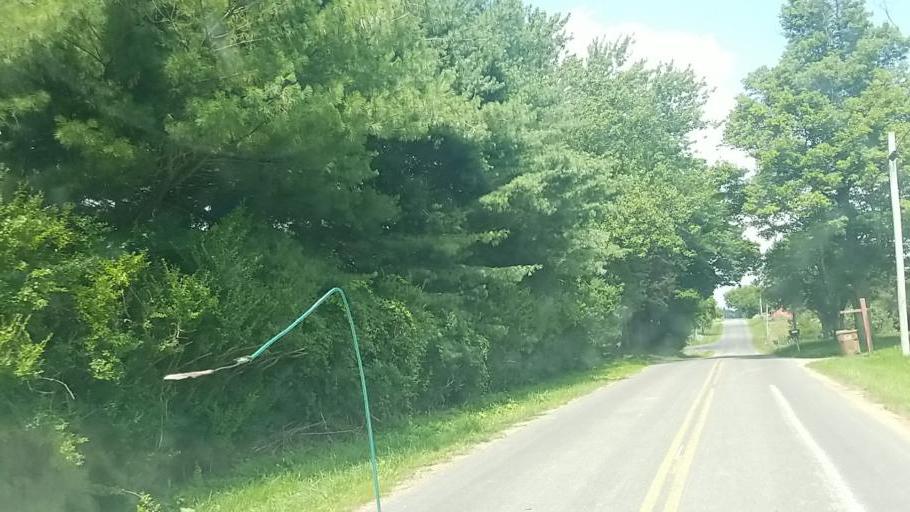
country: US
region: Ohio
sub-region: Medina County
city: Lodi
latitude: 41.0664
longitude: -82.0765
